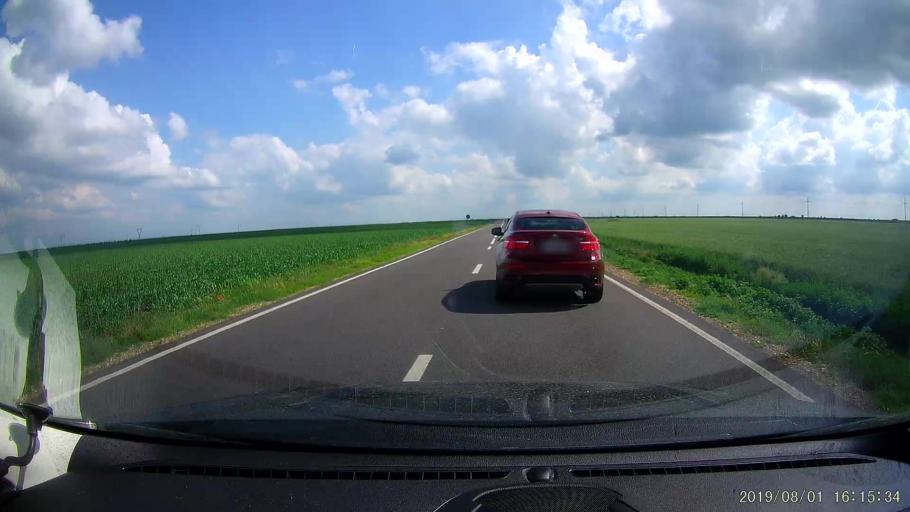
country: RO
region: Calarasi
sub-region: Comuna Stefan Voda
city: Stefan Voda
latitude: 44.3358
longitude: 27.3607
